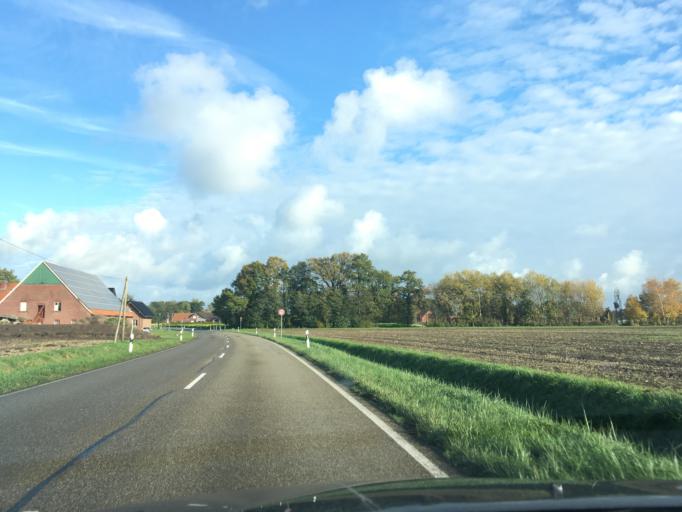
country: DE
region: North Rhine-Westphalia
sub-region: Regierungsbezirk Munster
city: Vreden
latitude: 52.0944
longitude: 6.8408
